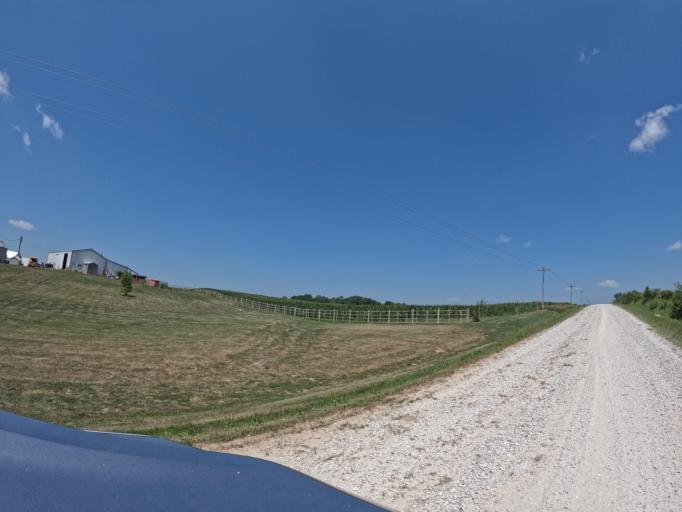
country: US
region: Iowa
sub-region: Keokuk County
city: Sigourney
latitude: 41.2953
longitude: -92.2191
